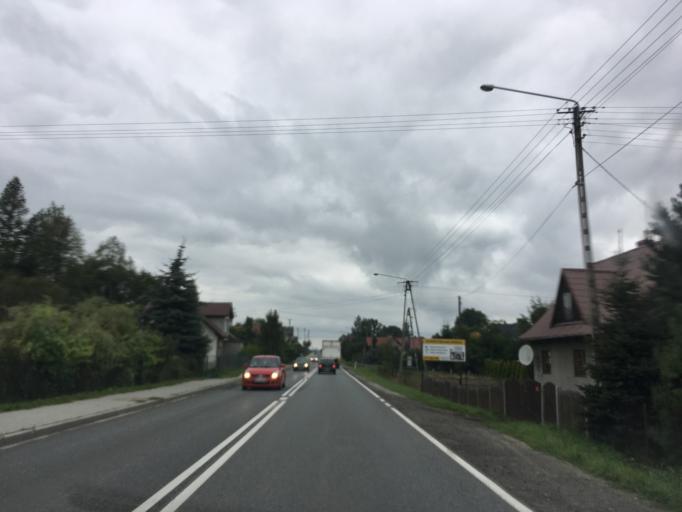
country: PL
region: Lesser Poland Voivodeship
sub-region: Powiat suski
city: Osielec
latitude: 49.6768
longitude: 19.7553
